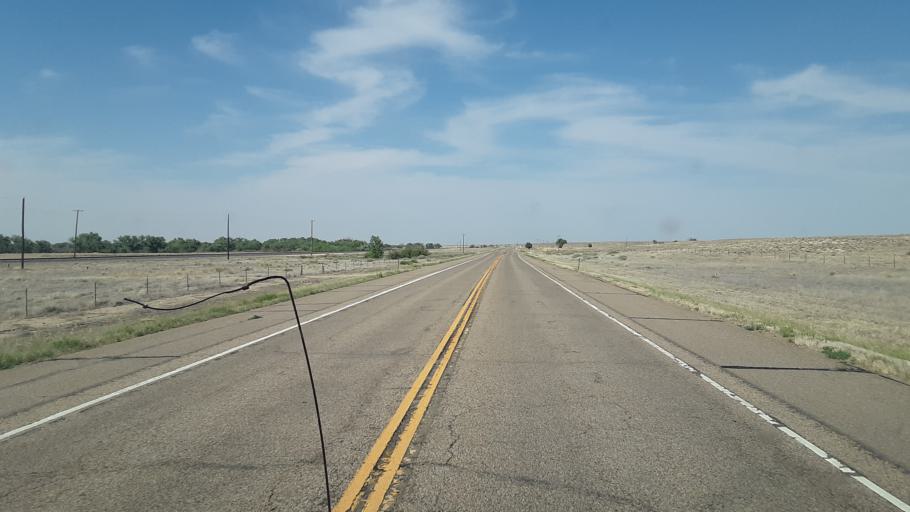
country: US
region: Colorado
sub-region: Otero County
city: La Junta
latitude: 38.0357
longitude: -103.4089
